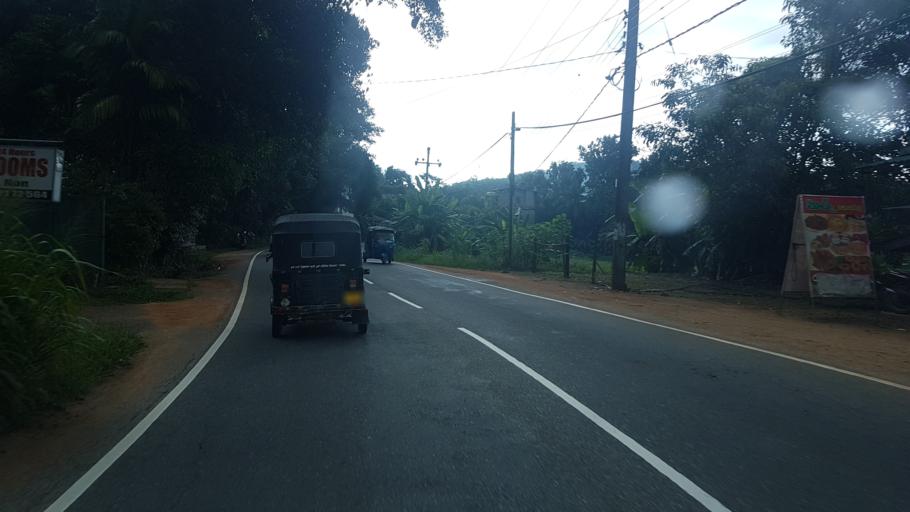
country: LK
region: Western
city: Hanwella Ihala
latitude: 6.9623
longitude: 80.2297
